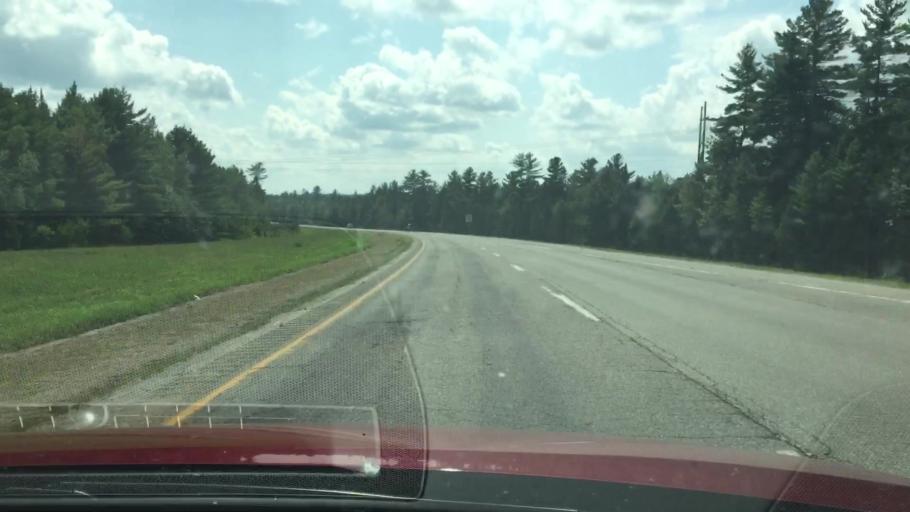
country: US
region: Maine
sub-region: Penobscot County
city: Medway
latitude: 45.5921
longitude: -68.5413
